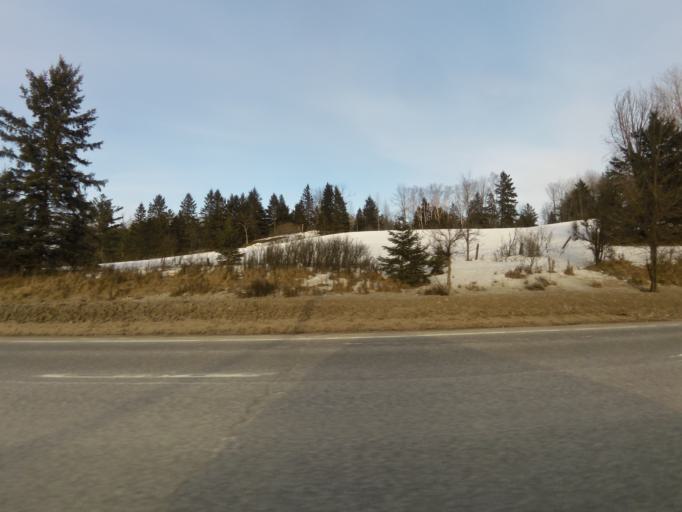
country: CA
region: Quebec
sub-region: Outaouais
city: Wakefield
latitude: 45.8517
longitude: -75.9963
